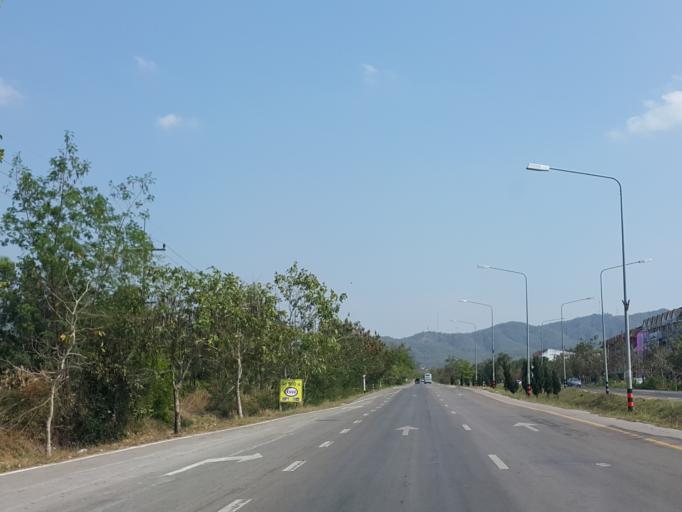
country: TH
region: Lampang
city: Lampang
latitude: 18.2715
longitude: 99.5255
